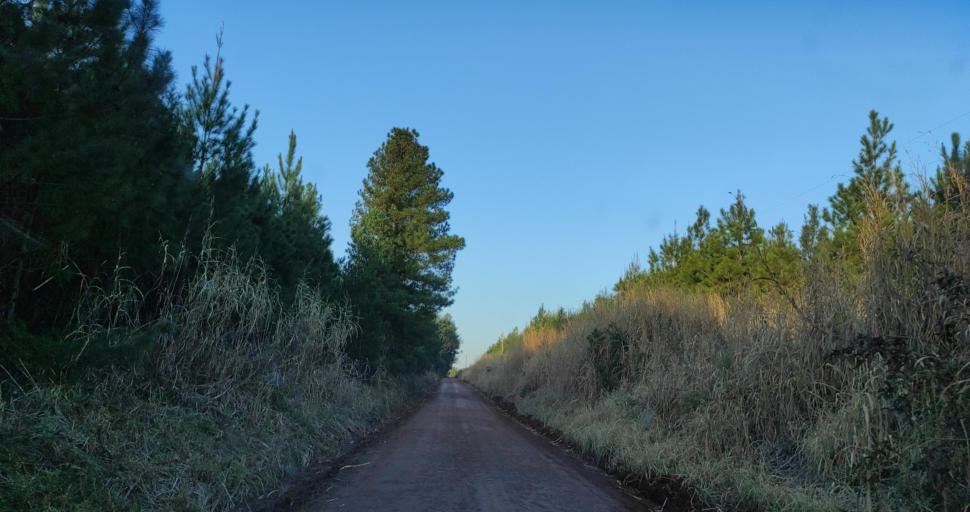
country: AR
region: Misiones
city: Capiovi
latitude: -26.8810
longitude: -55.1201
